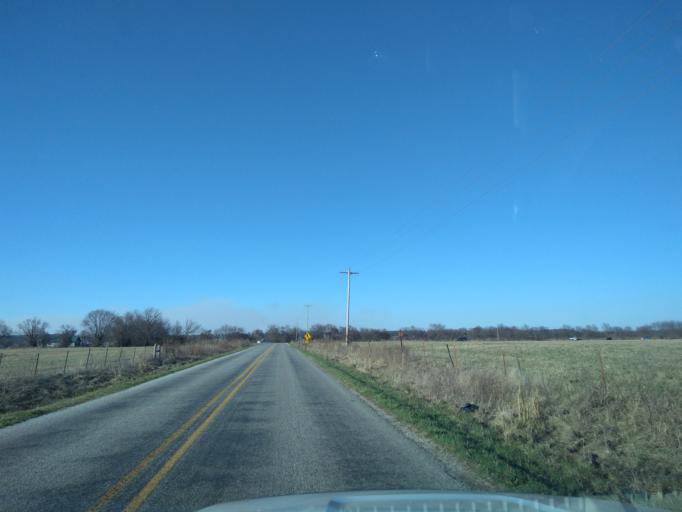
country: US
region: Arkansas
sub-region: Washington County
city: Lincoln
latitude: 36.0140
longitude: -94.3924
